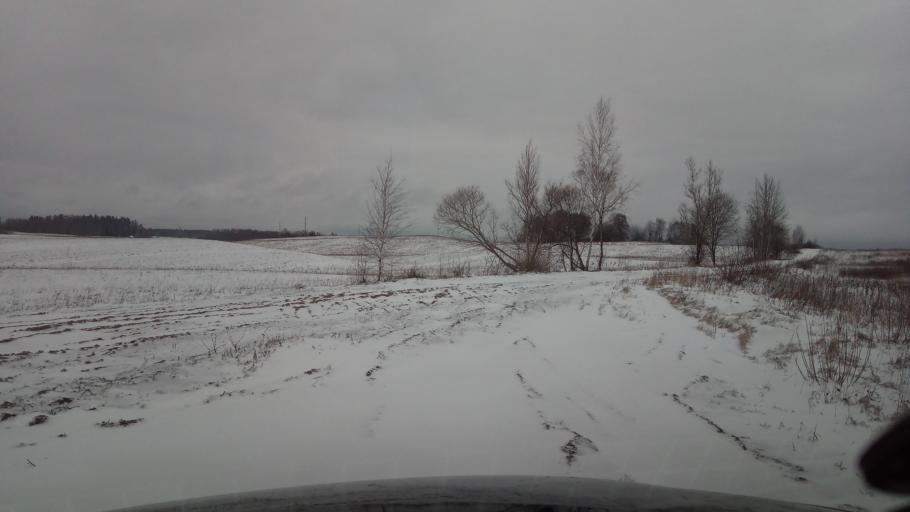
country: LT
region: Utenos apskritis
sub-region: Utena
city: Utena
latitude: 55.6102
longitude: 25.8657
